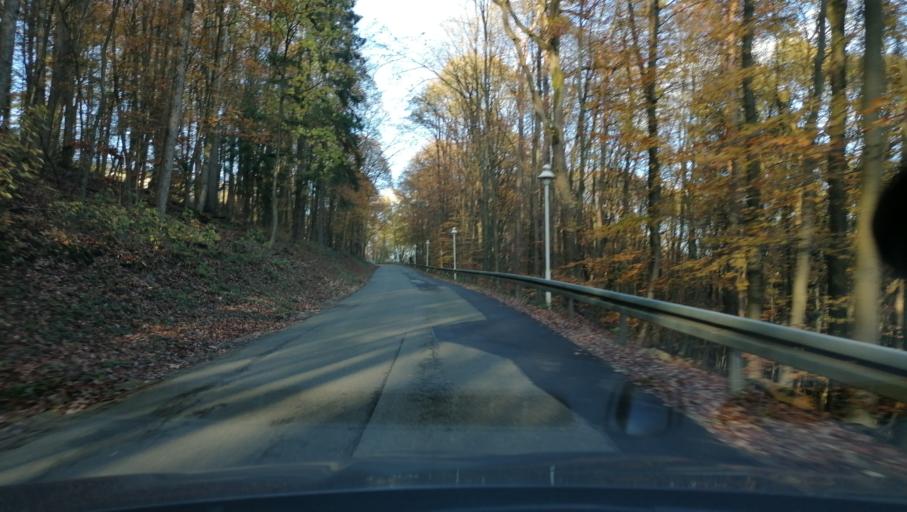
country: DE
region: North Rhine-Westphalia
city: Ennepetal
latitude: 51.2749
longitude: 7.3325
